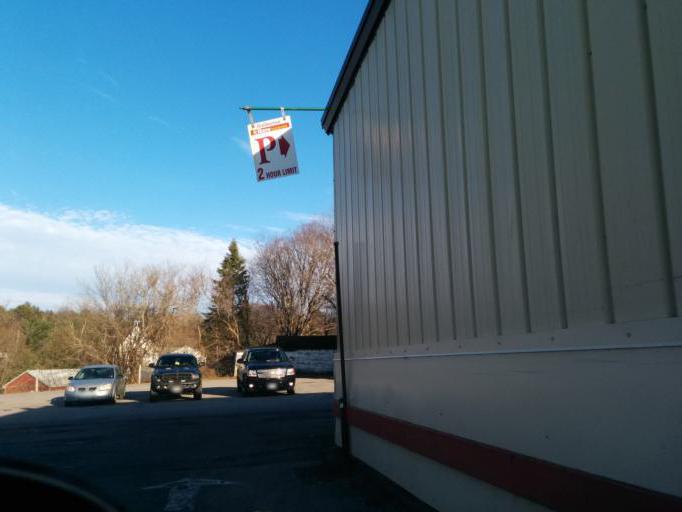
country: CA
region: Ontario
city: Bancroft
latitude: 45.0469
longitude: -78.5084
